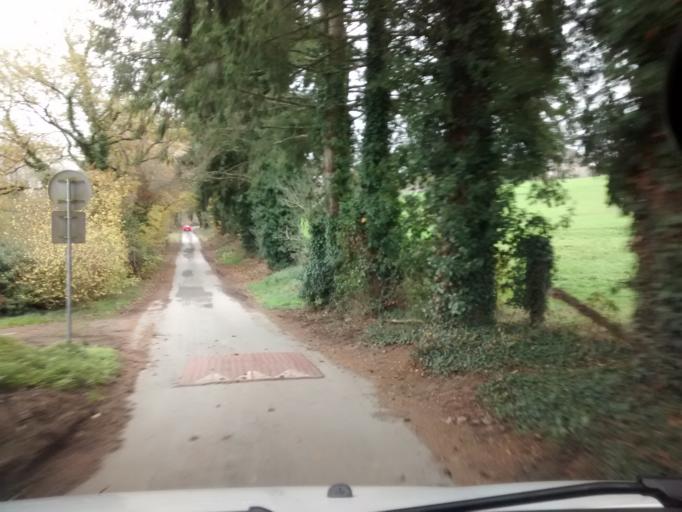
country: FR
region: Brittany
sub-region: Departement d'Ille-et-Vilaine
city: Argentre-du-Plessis
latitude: 48.0814
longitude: -1.1664
